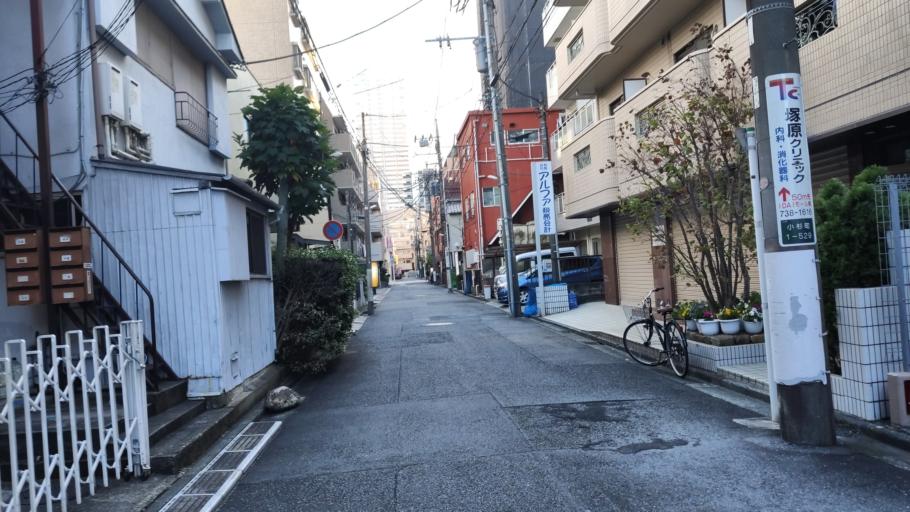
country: JP
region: Kanagawa
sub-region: Kawasaki-shi
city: Kawasaki
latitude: 35.5808
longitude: 139.6592
